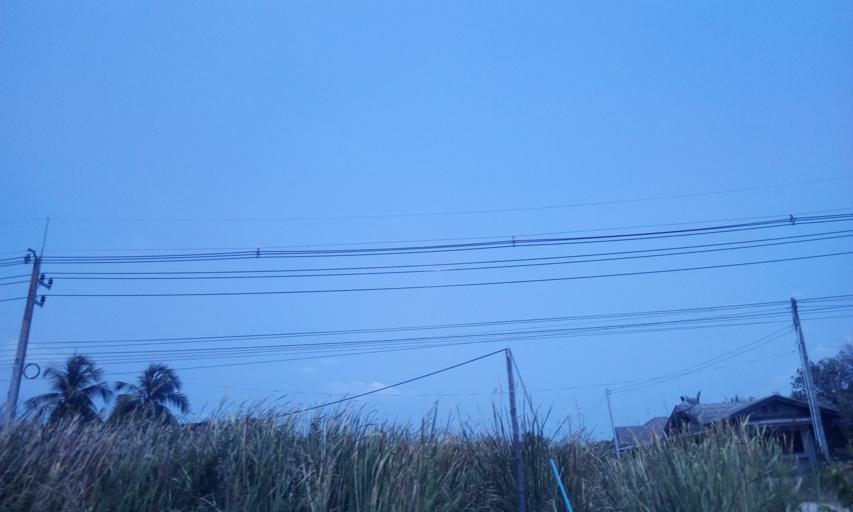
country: TH
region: Chachoengsao
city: Bang Nam Priao
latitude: 13.8411
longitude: 100.9895
